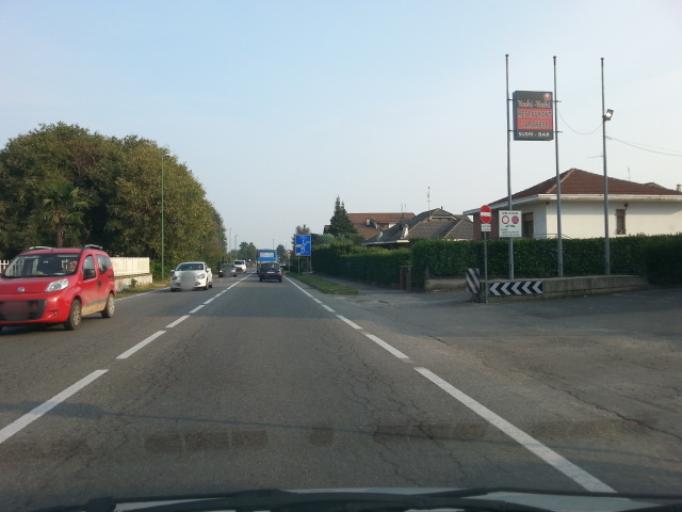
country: IT
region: Piedmont
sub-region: Provincia di Torino
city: Sangano
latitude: 45.0217
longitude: 7.4624
